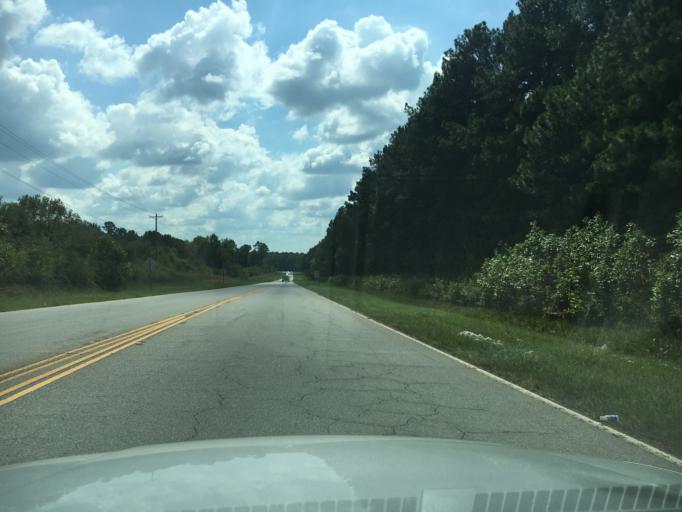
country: US
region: South Carolina
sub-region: Greenwood County
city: Greenwood
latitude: 34.1728
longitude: -82.1827
